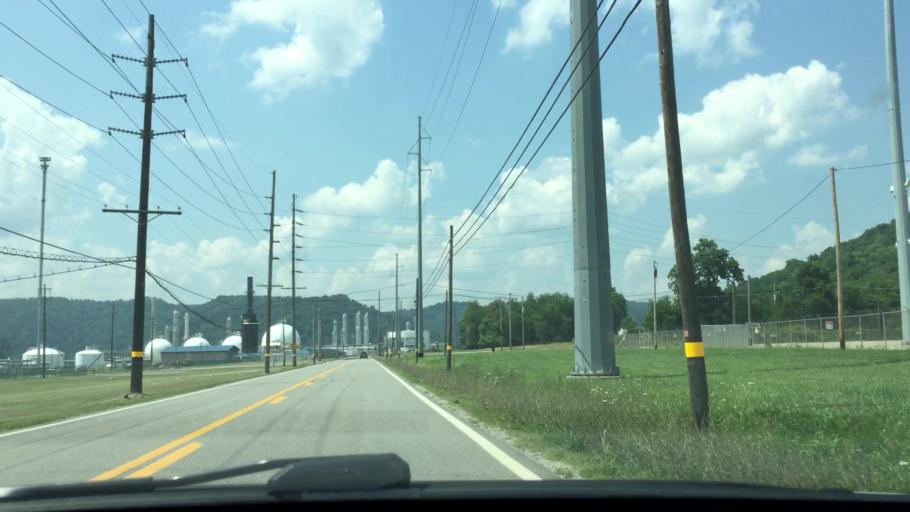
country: US
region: West Virginia
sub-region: Wetzel County
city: New Martinsville
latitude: 39.7542
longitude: -80.8560
